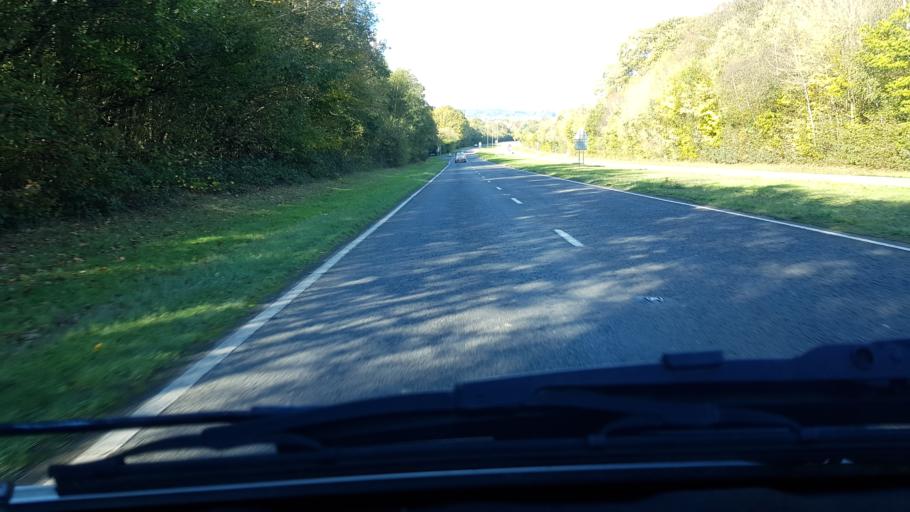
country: GB
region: England
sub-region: Surrey
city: Ockley
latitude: 51.1477
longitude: -0.3289
